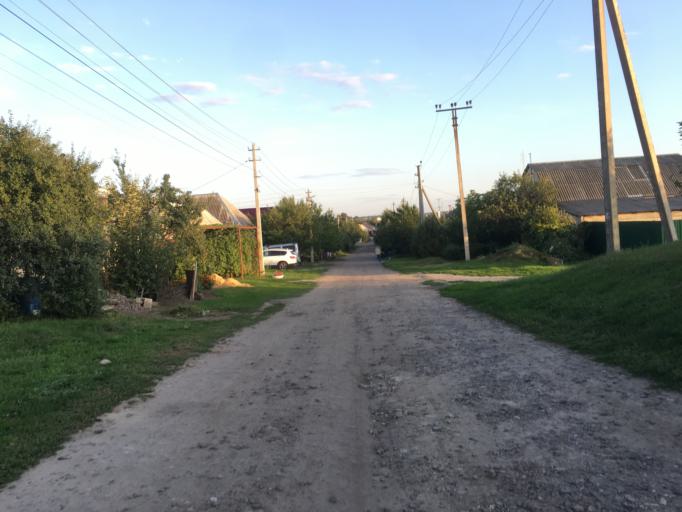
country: RU
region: Voronezj
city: Rossosh'
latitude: 50.2116
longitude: 39.5258
